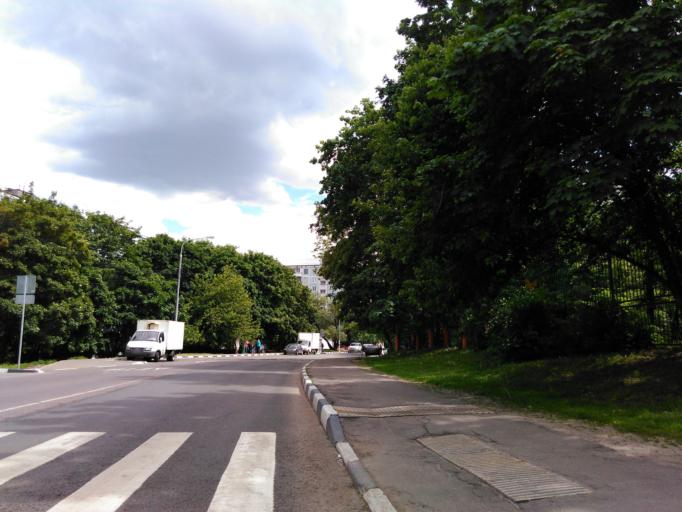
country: RU
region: Moscow
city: Zyuzino
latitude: 55.6611
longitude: 37.5709
